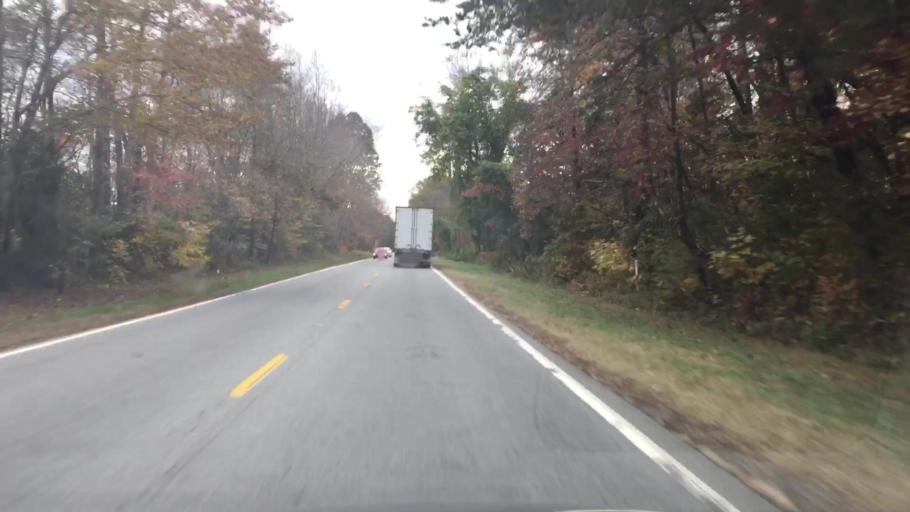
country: US
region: North Carolina
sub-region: Guilford County
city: Stokesdale
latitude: 36.2303
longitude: -80.0250
